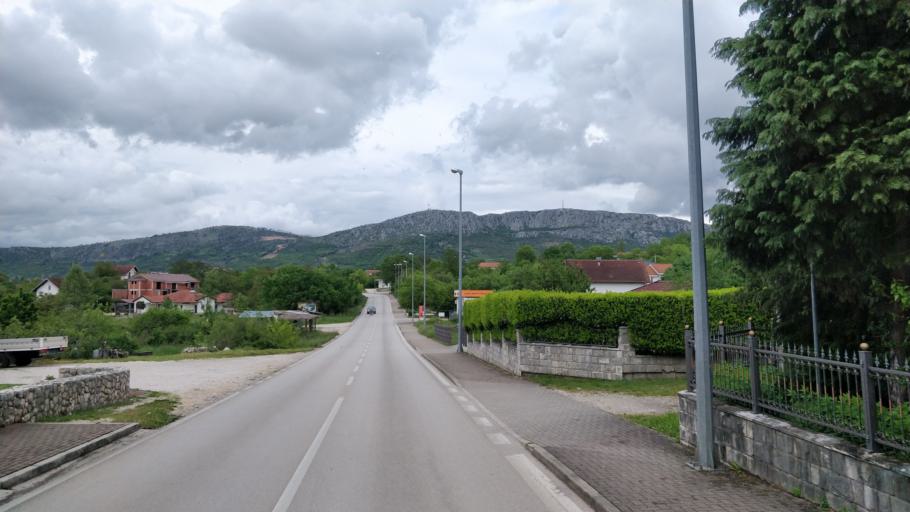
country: BA
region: Federation of Bosnia and Herzegovina
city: Ljubuski
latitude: 43.1850
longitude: 17.5287
